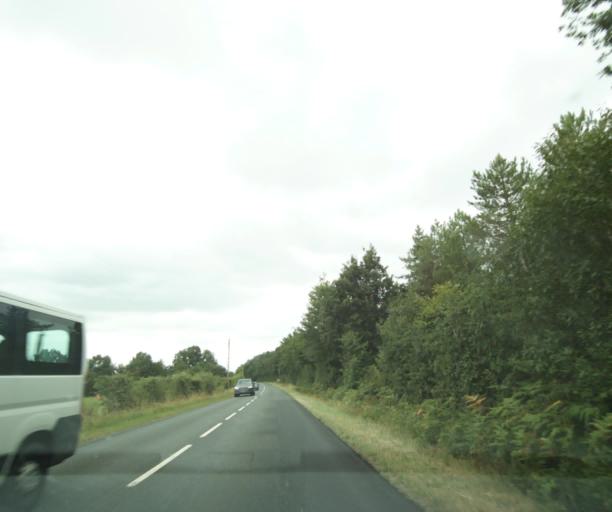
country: FR
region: Pays de la Loire
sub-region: Departement de la Sarthe
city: Precigne
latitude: 47.7927
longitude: -0.3208
